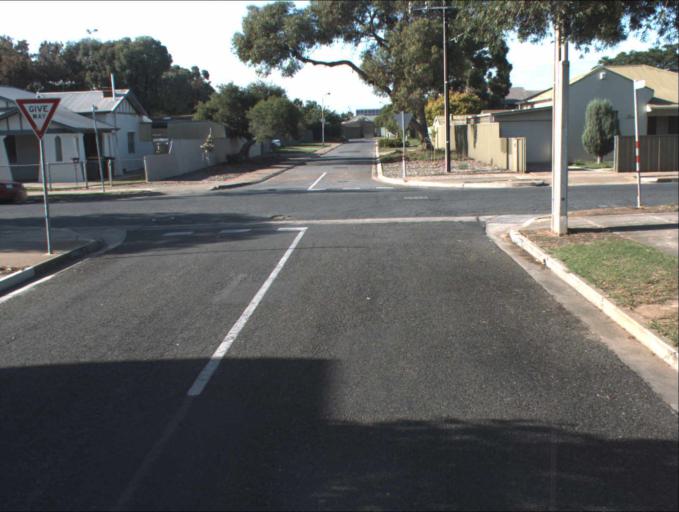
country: AU
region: South Australia
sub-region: Prospect
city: Prospect
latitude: -34.8895
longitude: 138.5784
